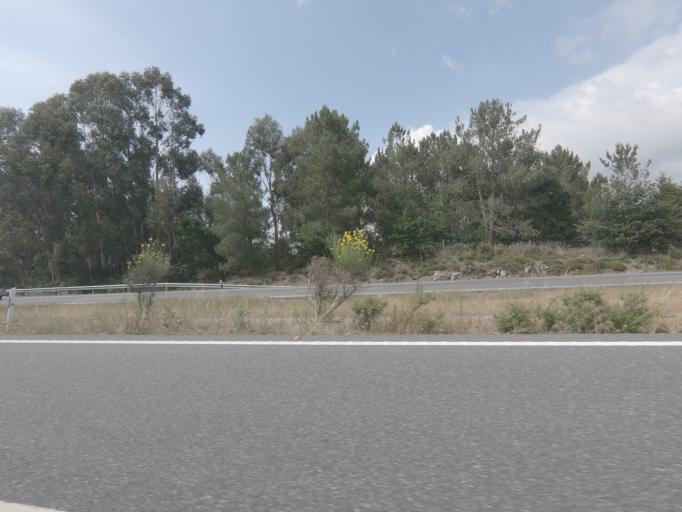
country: ES
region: Galicia
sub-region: Provincia de Pontevedra
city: Covelo
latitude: 42.2011
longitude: -8.2886
